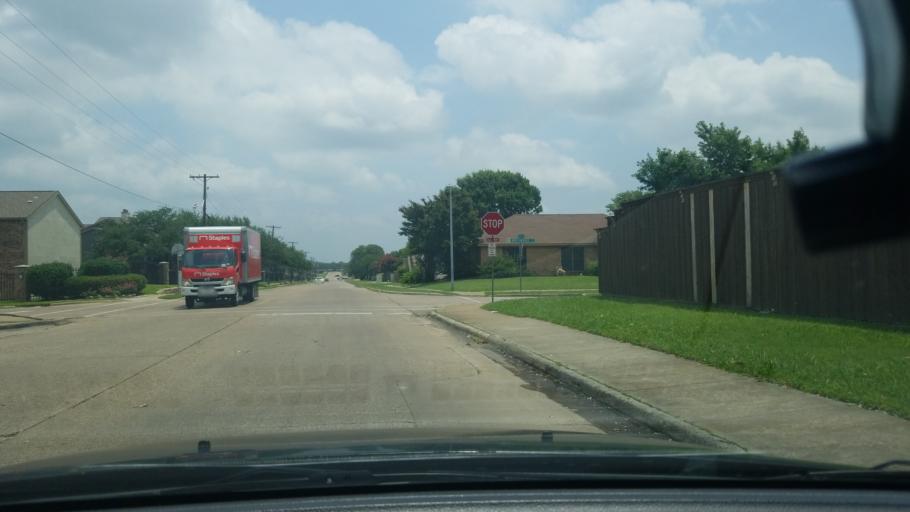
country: US
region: Texas
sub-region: Dallas County
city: Mesquite
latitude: 32.8051
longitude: -96.6158
